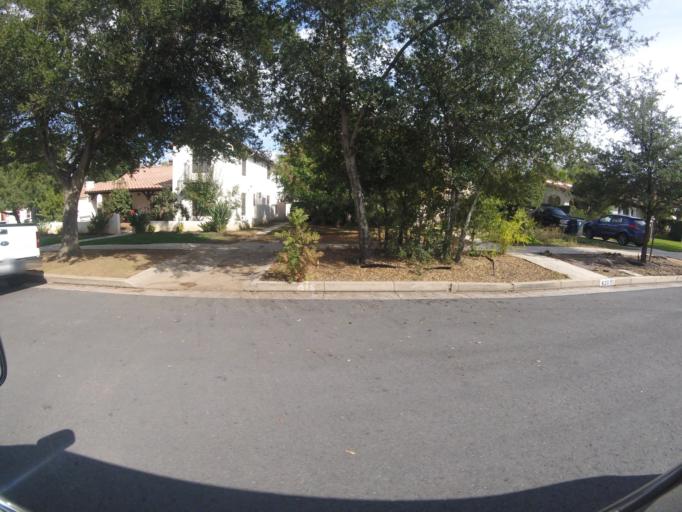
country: US
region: California
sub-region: San Bernardino County
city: Redlands
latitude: 34.0438
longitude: -117.1806
